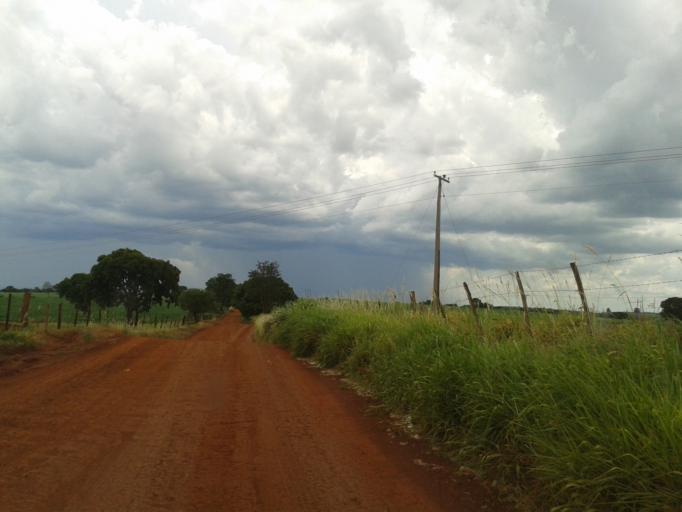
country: BR
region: Minas Gerais
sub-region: Centralina
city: Centralina
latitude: -18.7070
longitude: -49.2158
